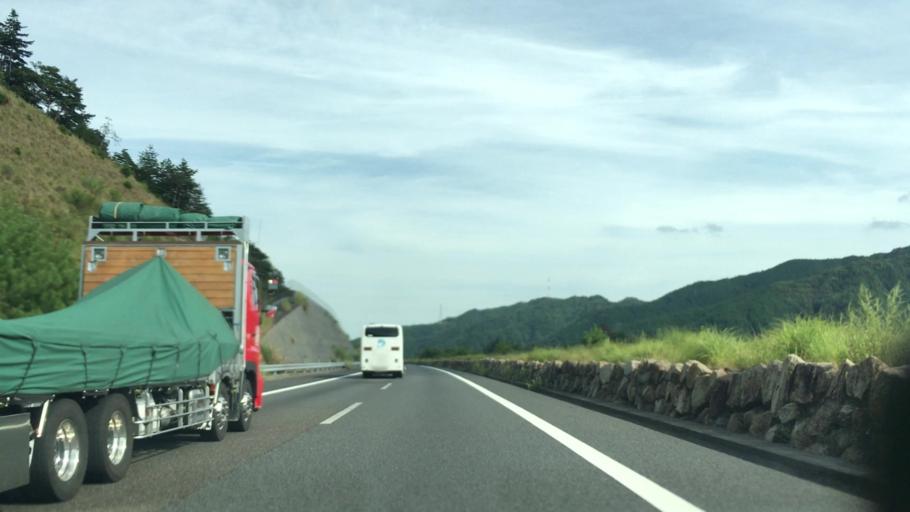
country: JP
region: Shiga Prefecture
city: Kusatsu
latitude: 34.9381
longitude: 136.0364
